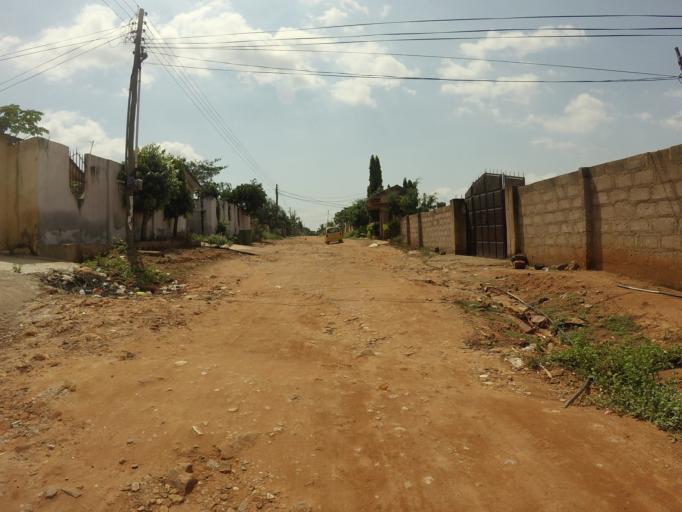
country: GH
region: Greater Accra
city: Gbawe
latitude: 5.6240
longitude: -0.3078
